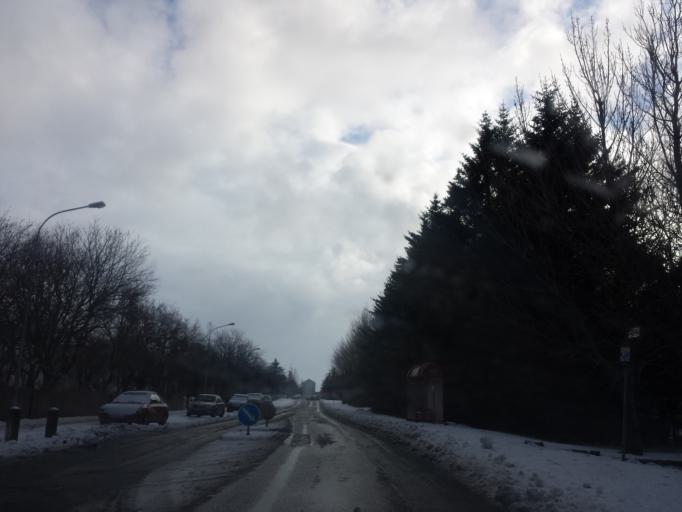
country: IS
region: Capital Region
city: Reykjavik
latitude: 64.1383
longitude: -21.9124
